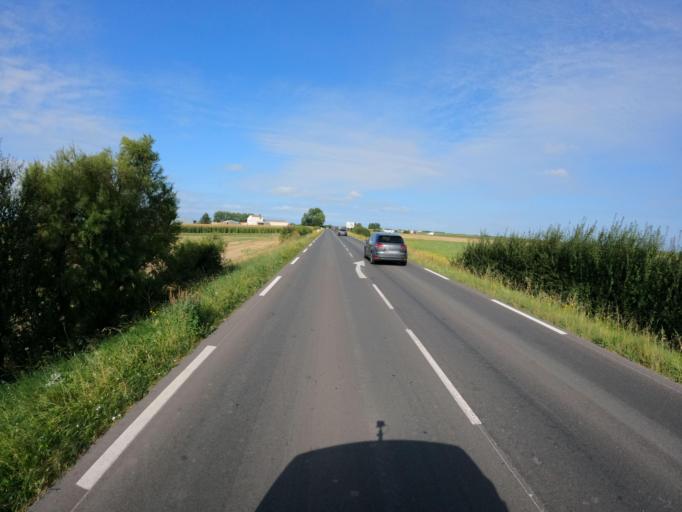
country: FR
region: Pays de la Loire
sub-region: Departement de la Vendee
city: Triaize
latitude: 46.3376
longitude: -1.2771
